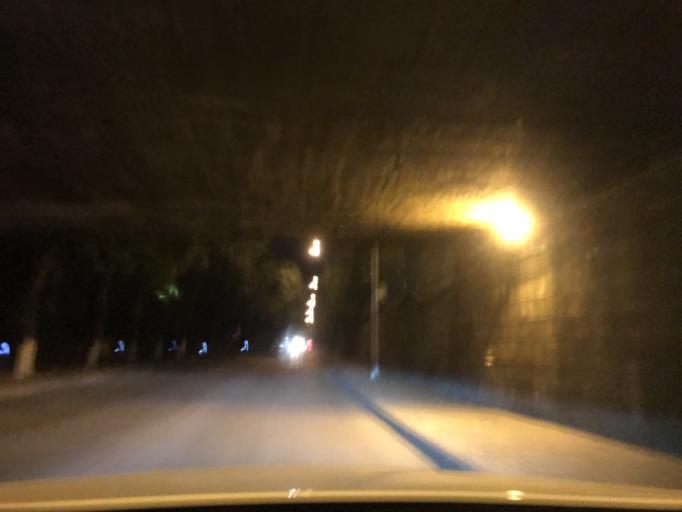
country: CN
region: Sichuan
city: Mianyang
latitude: 31.4549
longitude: 104.7466
